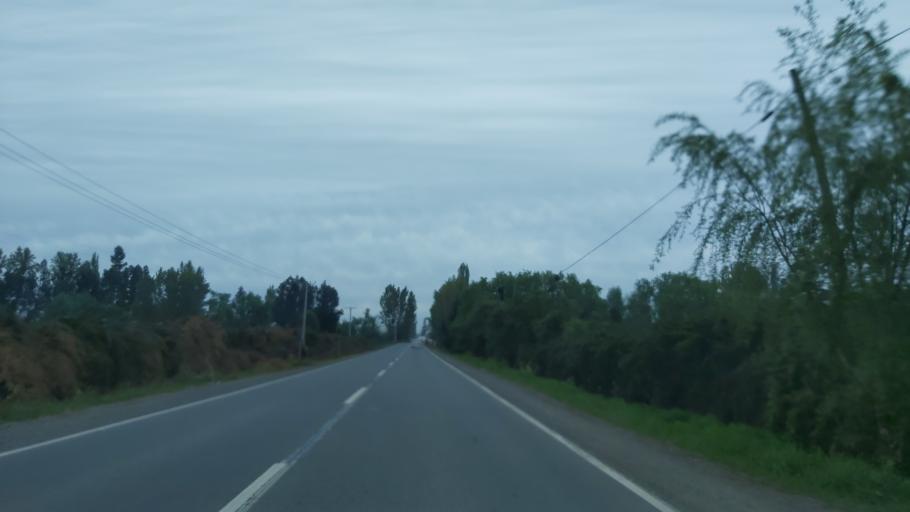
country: CL
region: Maule
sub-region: Provincia de Linares
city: Colbun
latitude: -35.7492
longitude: -71.4940
